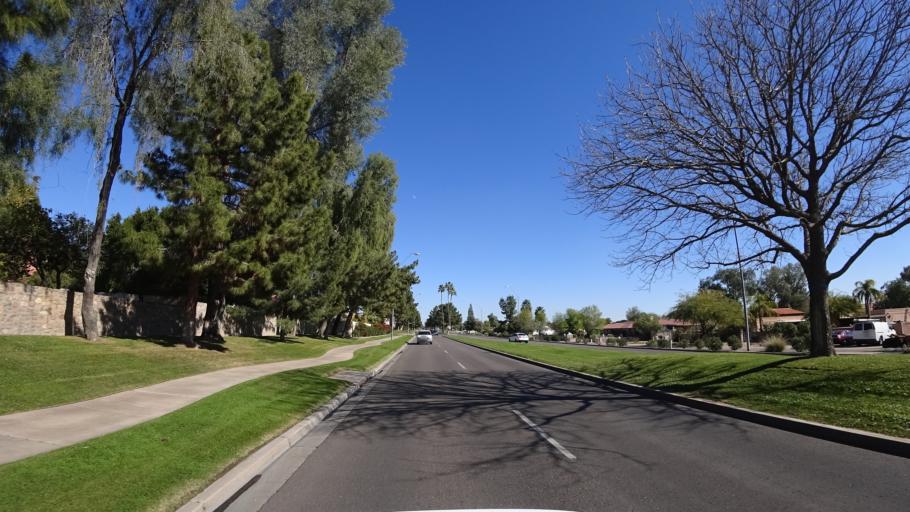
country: US
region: Arizona
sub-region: Maricopa County
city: Peoria
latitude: 33.6528
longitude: -112.2129
